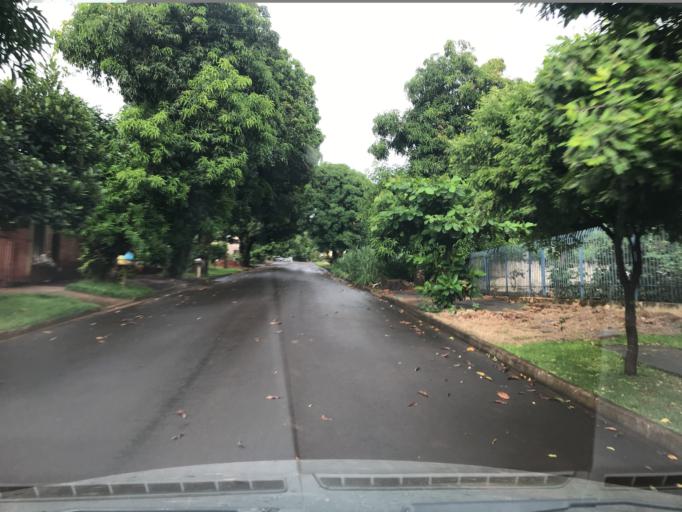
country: BR
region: Parana
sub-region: Palotina
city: Palotina
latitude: -24.2931
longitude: -53.8480
